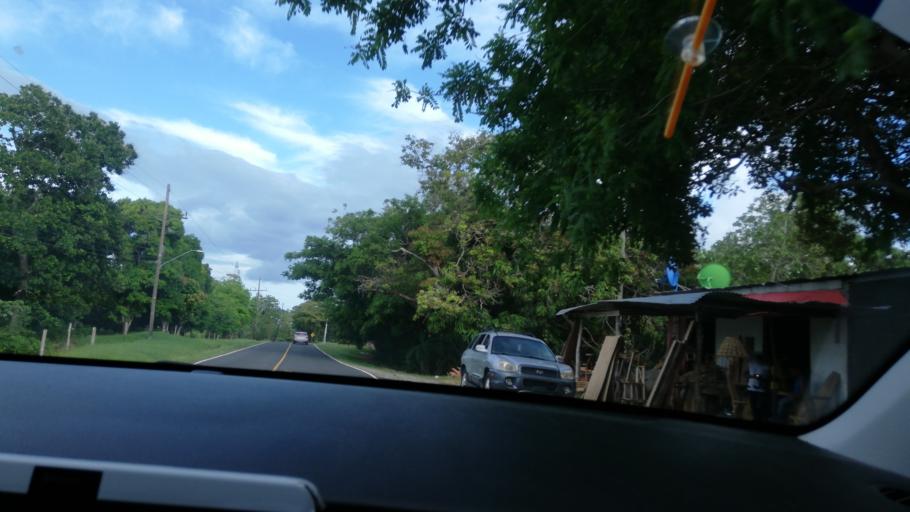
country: PA
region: Panama
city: Las Colinas
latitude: 8.4929
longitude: -80.0252
